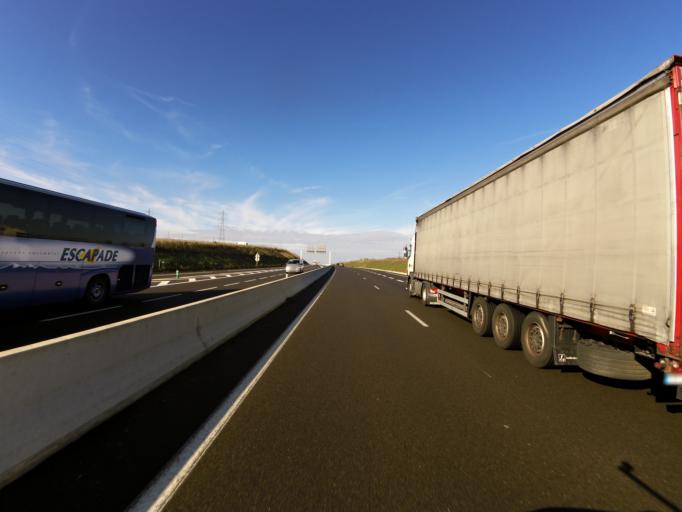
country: FR
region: Champagne-Ardenne
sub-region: Departement de la Marne
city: Bezannes
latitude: 49.2085
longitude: 4.0072
